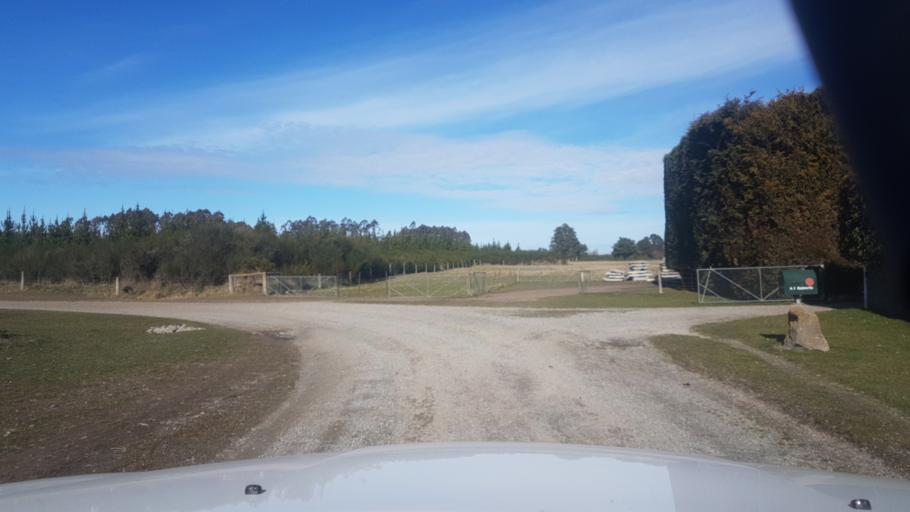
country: NZ
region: Canterbury
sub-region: Timaru District
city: Pleasant Point
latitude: -44.1365
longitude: 171.2736
